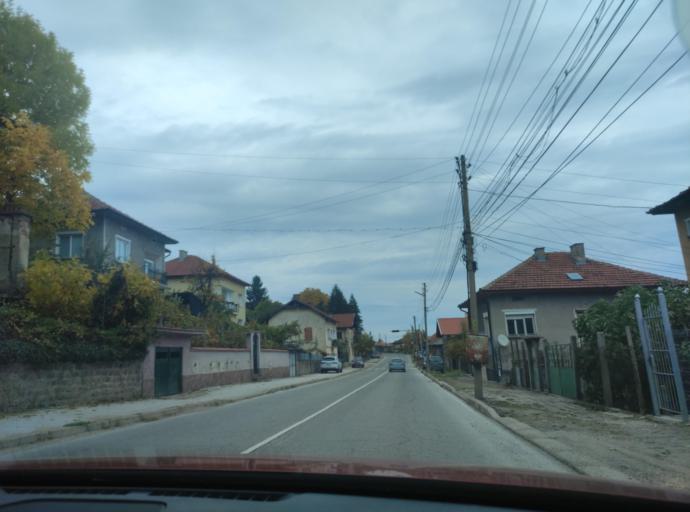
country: BG
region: Montana
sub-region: Obshtina Berkovitsa
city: Berkovitsa
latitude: 43.2023
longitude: 23.1614
